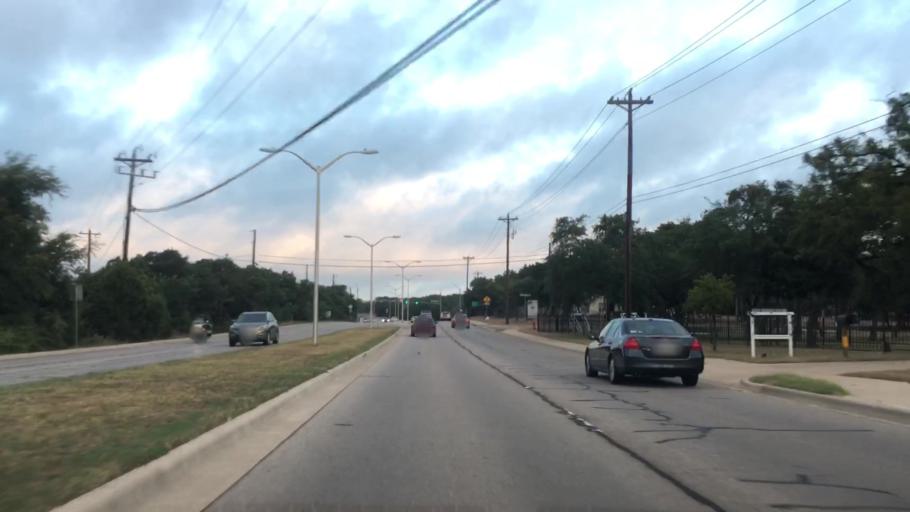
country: US
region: Texas
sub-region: Williamson County
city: Cedar Park
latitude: 30.5082
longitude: -97.7845
